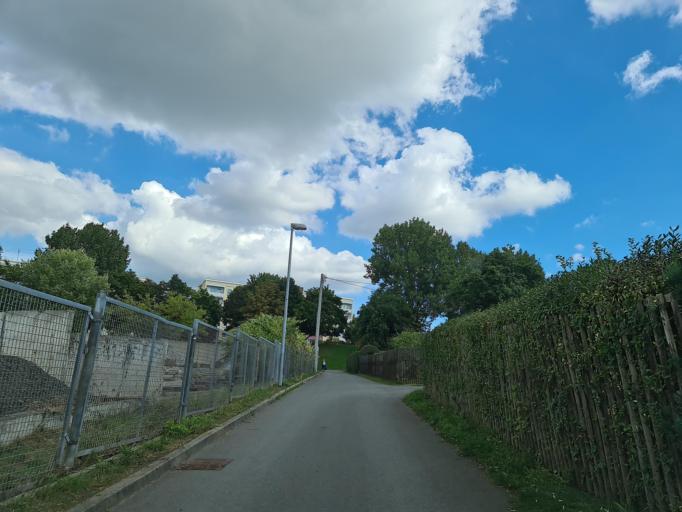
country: DE
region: Saxony
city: Plauen
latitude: 50.4847
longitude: 12.1445
